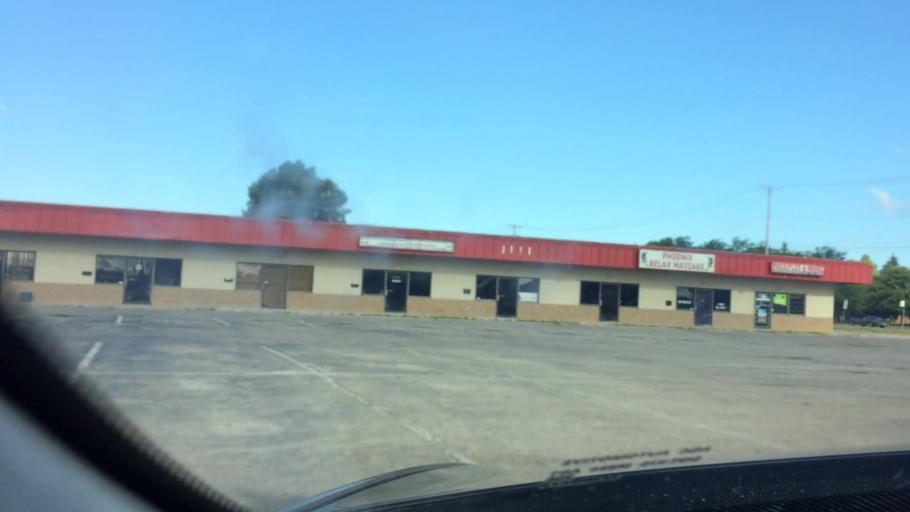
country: US
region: Ohio
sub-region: Lucas County
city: Ottawa Hills
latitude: 41.6381
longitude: -83.6654
